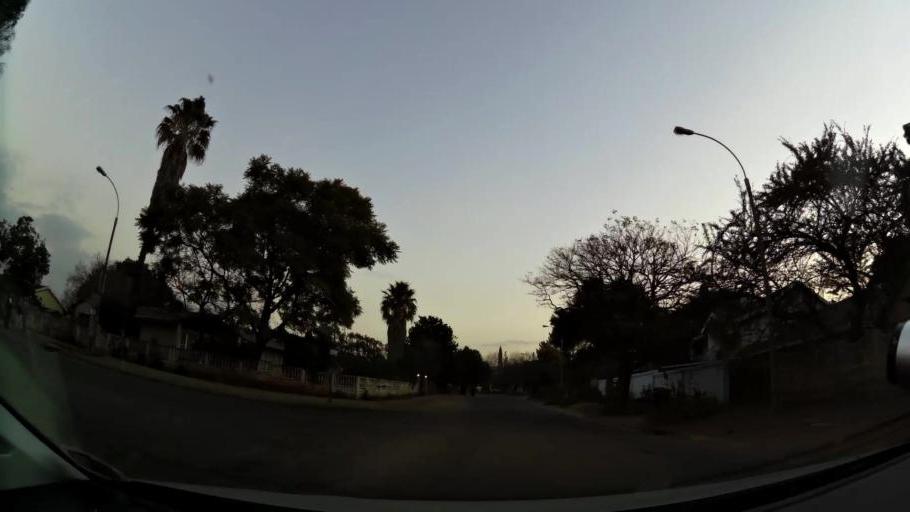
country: ZA
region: Gauteng
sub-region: Ekurhuleni Metropolitan Municipality
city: Tembisa
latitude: -26.0489
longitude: 28.2411
